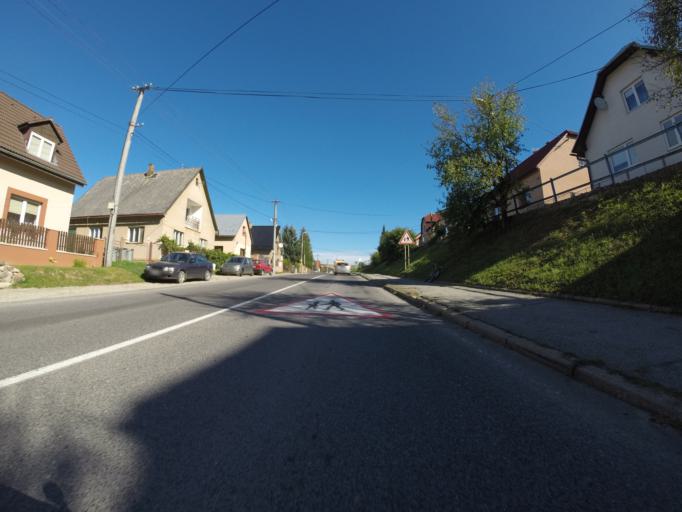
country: SK
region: Trenciansky
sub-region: Okres Povazska Bystrica
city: Povazska Bystrica
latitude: 49.0814
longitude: 18.4074
